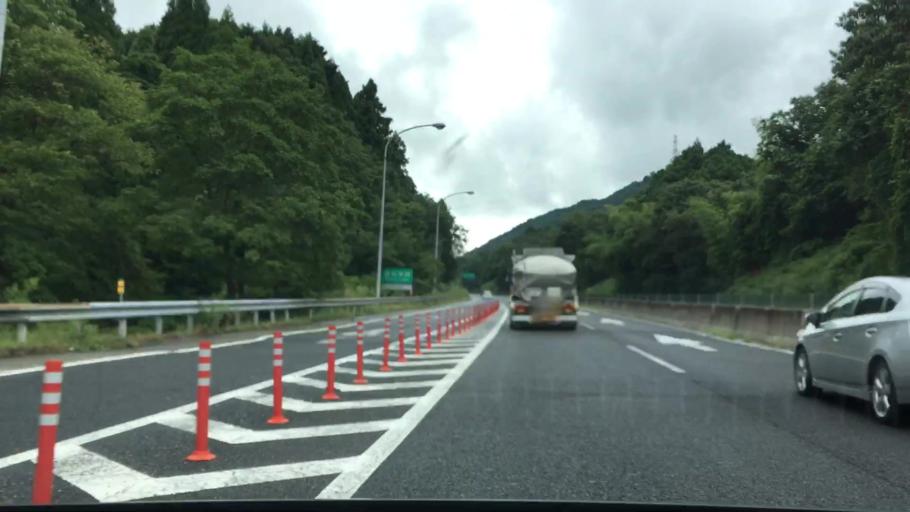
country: JP
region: Hyogo
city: Yamazakicho-nakabirose
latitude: 35.0327
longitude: 134.4842
